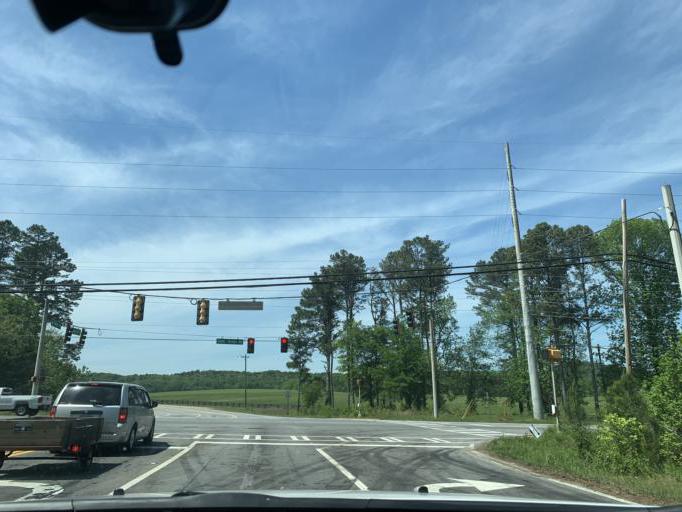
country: US
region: Georgia
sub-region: Forsyth County
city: Cumming
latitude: 34.2681
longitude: -84.0559
